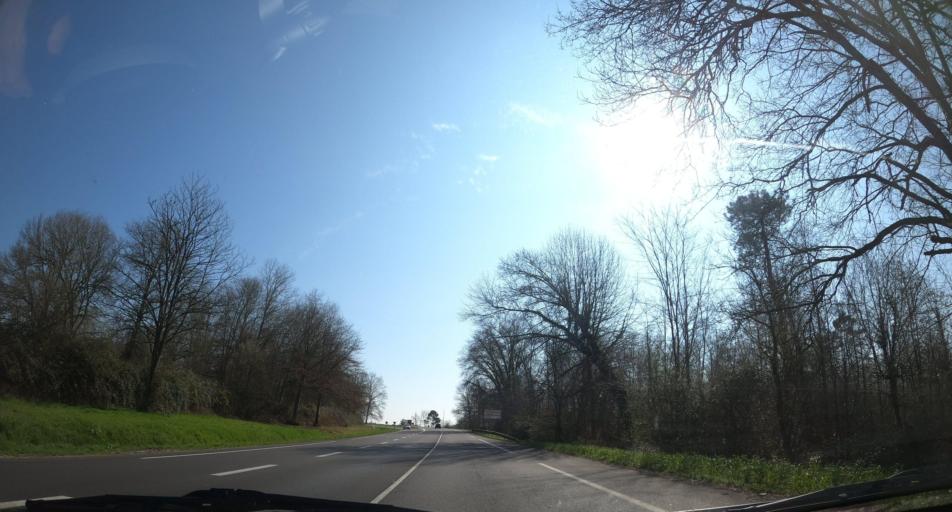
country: FR
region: Aquitaine
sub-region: Departement des Landes
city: Saint-Pierre-du-Mont
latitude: 43.8690
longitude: -0.5161
